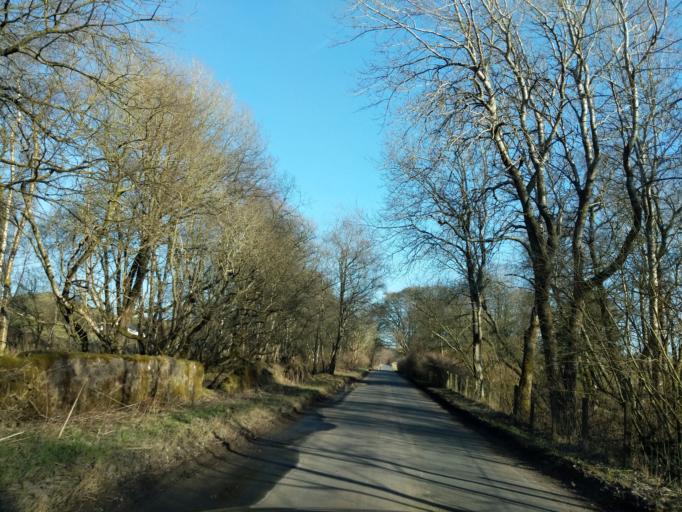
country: GB
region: Scotland
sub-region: The Scottish Borders
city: West Linton
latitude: 55.7188
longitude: -3.4268
